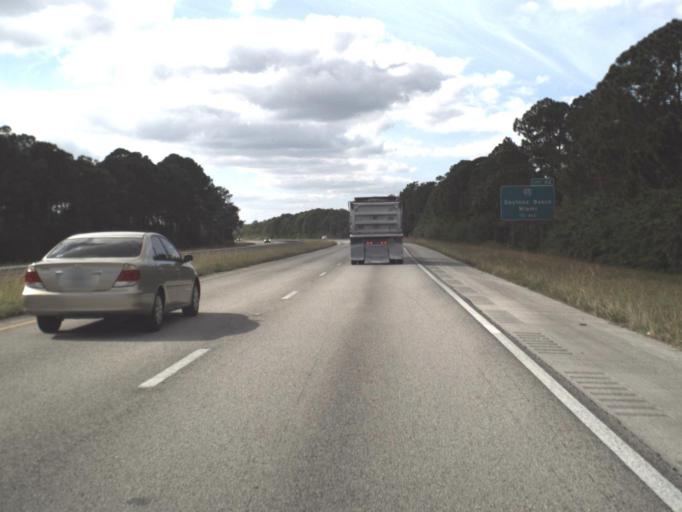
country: US
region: Florida
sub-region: Brevard County
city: Sharpes
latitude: 28.4112
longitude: -80.8055
